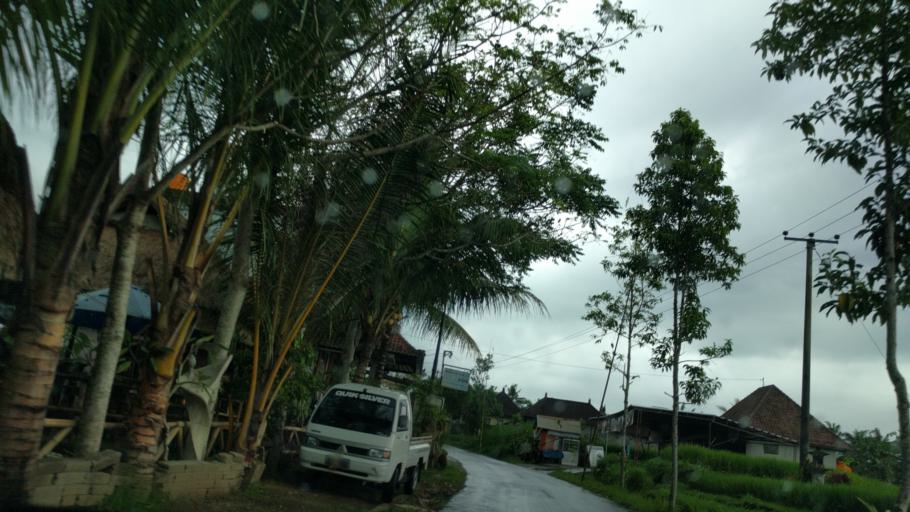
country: ID
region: Bali
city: Bunutan
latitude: -8.4640
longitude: 115.2598
